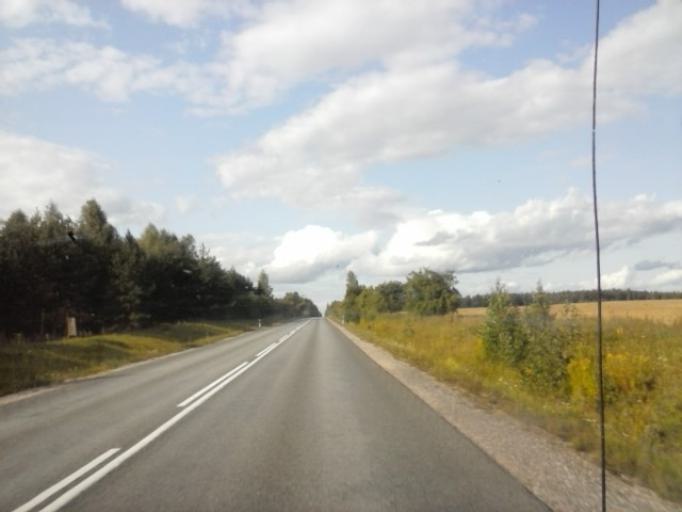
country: LV
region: Valmieras Rajons
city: Valmiera
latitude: 57.4795
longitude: 25.4078
